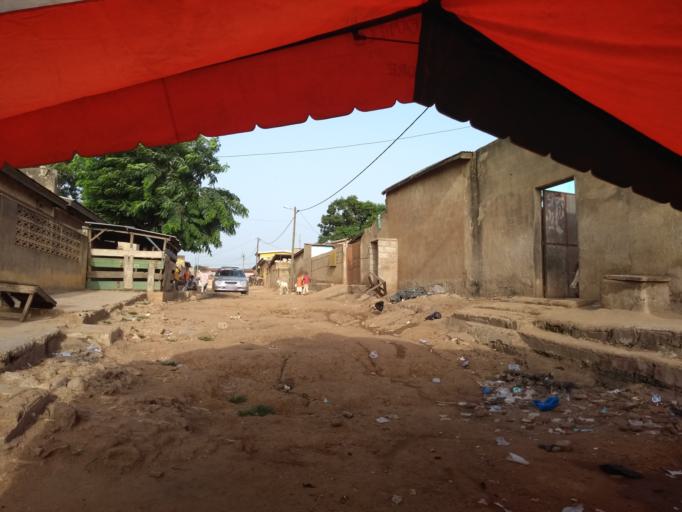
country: CI
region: Vallee du Bandama
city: Bouake
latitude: 7.7085
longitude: -5.0278
